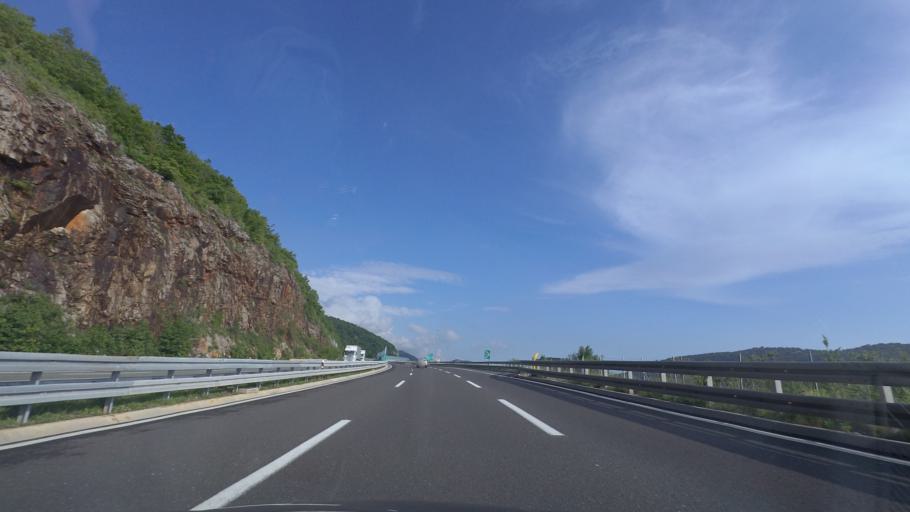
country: HR
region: Primorsko-Goranska
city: Skrljevo
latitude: 45.3690
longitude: 14.5465
